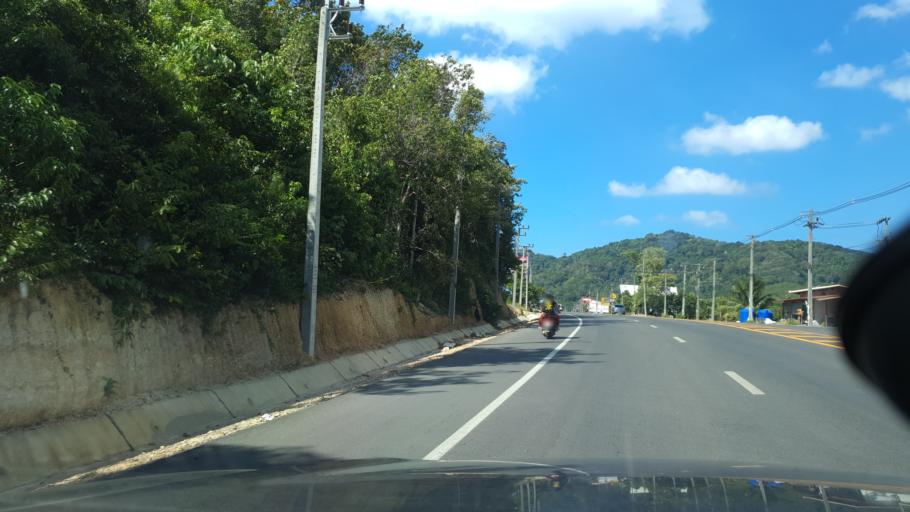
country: TH
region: Phangnga
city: Ban Ao Nang
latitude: 8.0422
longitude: 98.8466
